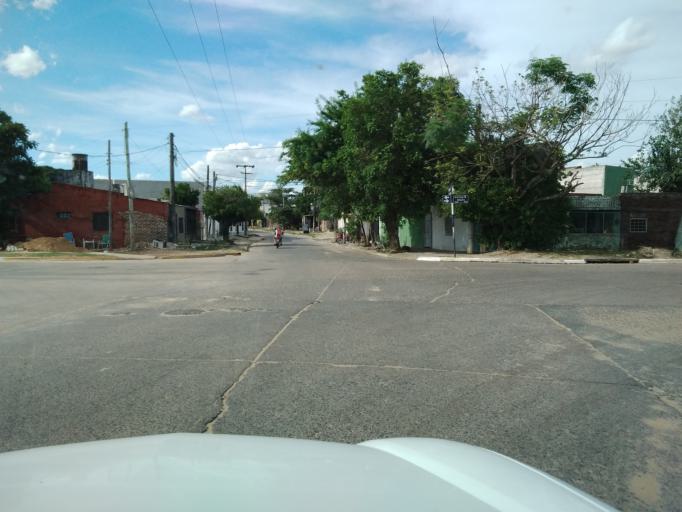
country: AR
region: Corrientes
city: Corrientes
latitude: -27.4831
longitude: -58.8496
